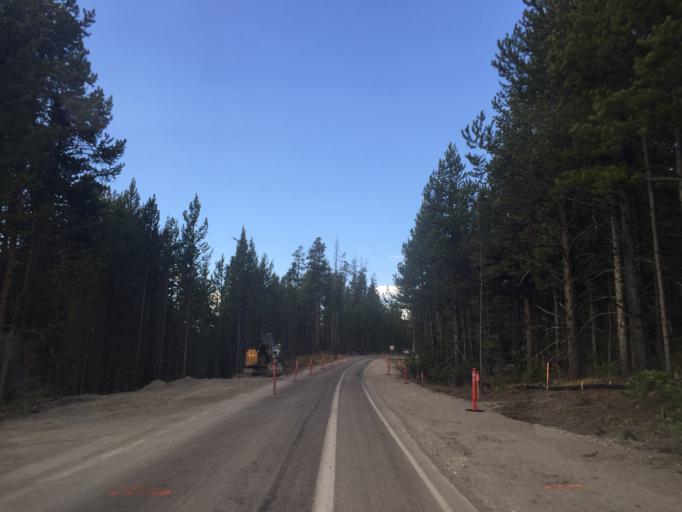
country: US
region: Montana
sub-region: Gallatin County
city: West Yellowstone
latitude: 44.7341
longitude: -110.4860
